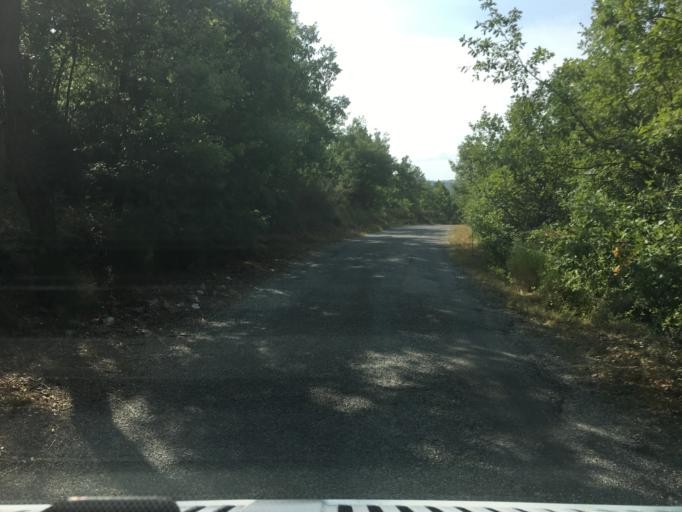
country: FR
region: Provence-Alpes-Cote d'Azur
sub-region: Departement des Alpes-de-Haute-Provence
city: Mallemoisson
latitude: 43.9221
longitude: 6.1913
